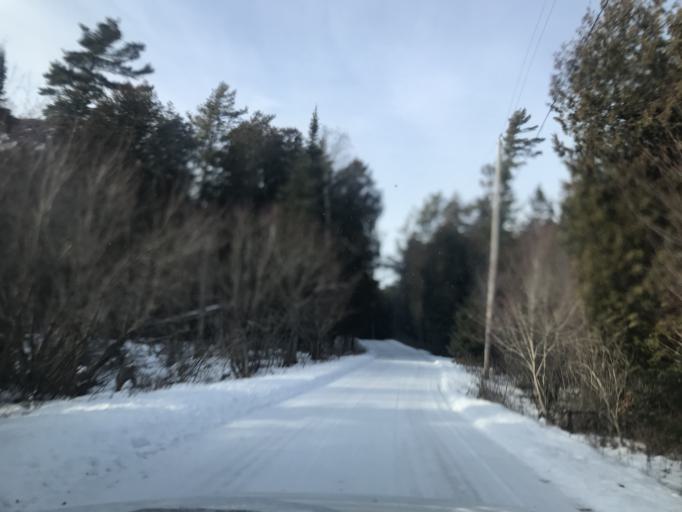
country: US
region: Wisconsin
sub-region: Door County
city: Sturgeon Bay
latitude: 45.1491
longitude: -87.0356
